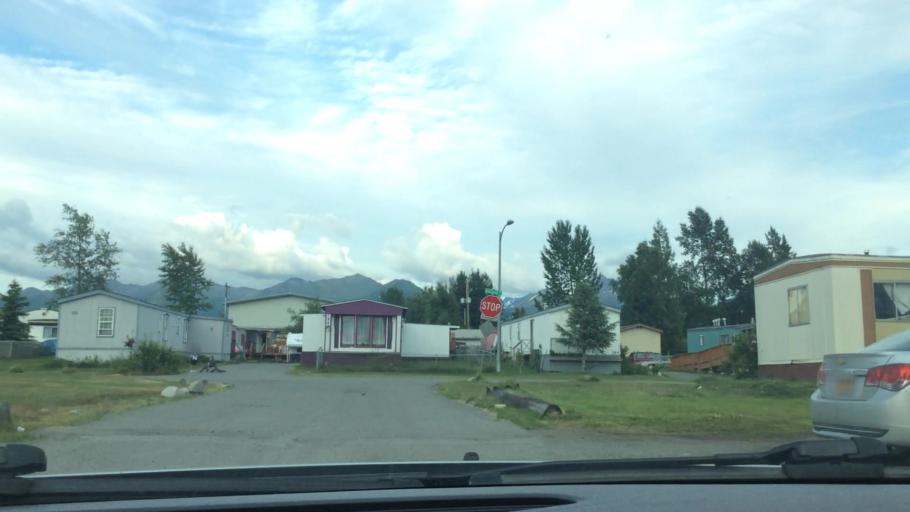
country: US
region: Alaska
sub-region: Anchorage Municipality
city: Anchorage
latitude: 61.1337
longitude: -149.8512
